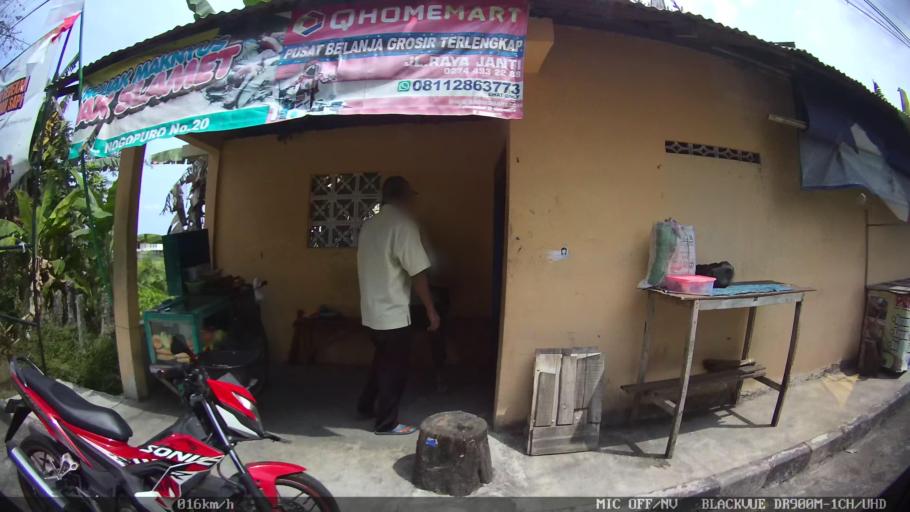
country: ID
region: Daerah Istimewa Yogyakarta
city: Depok
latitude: -7.7848
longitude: 110.4031
